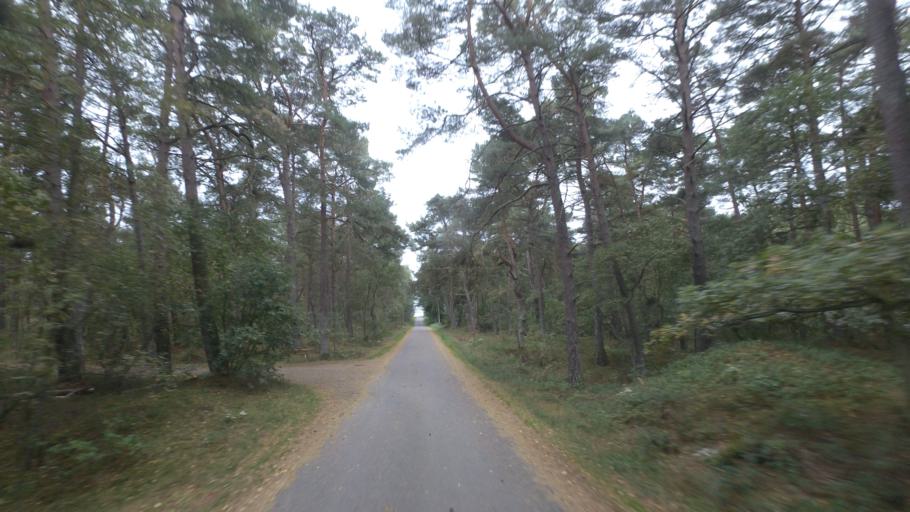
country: DK
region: Capital Region
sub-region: Bornholm Kommune
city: Nexo
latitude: 54.9980
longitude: 15.0388
